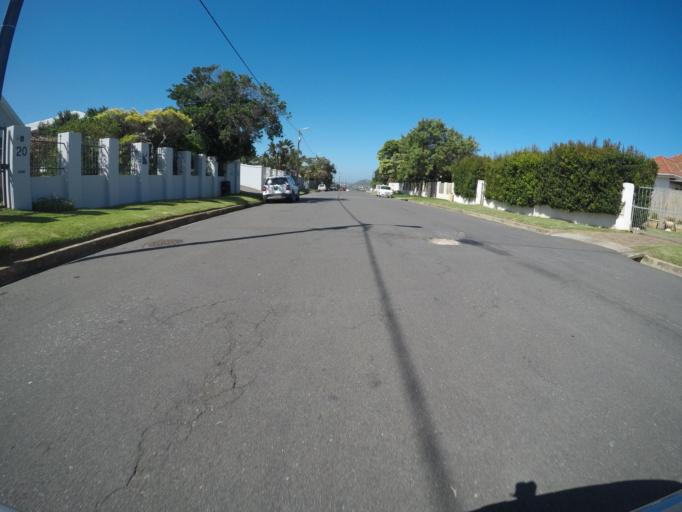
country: ZA
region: Eastern Cape
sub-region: Buffalo City Metropolitan Municipality
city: East London
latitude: -32.9872
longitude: 27.9434
